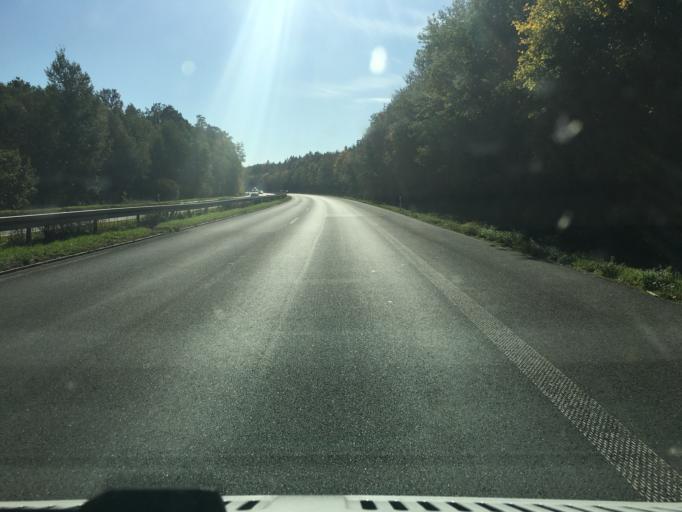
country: DE
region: Saxony
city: Dennheritz
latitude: 50.7994
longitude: 12.4548
